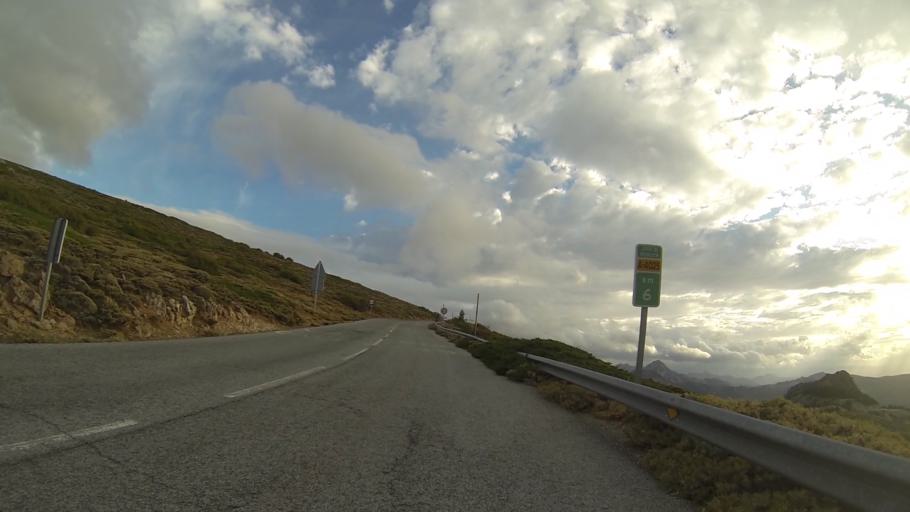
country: ES
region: Andalusia
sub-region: Provincia de Granada
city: Guejar-Sierra
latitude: 37.1218
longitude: -3.4311
